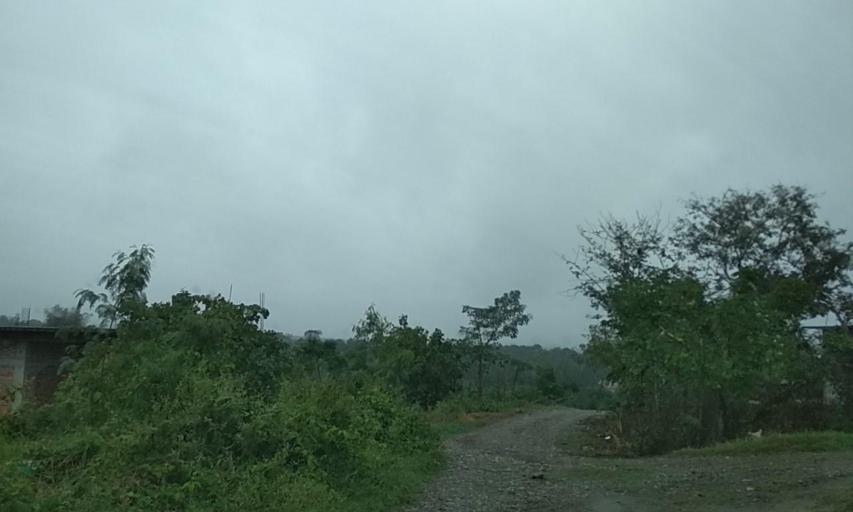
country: MX
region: Veracruz
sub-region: Papantla
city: El Chote
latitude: 20.3571
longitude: -97.3434
